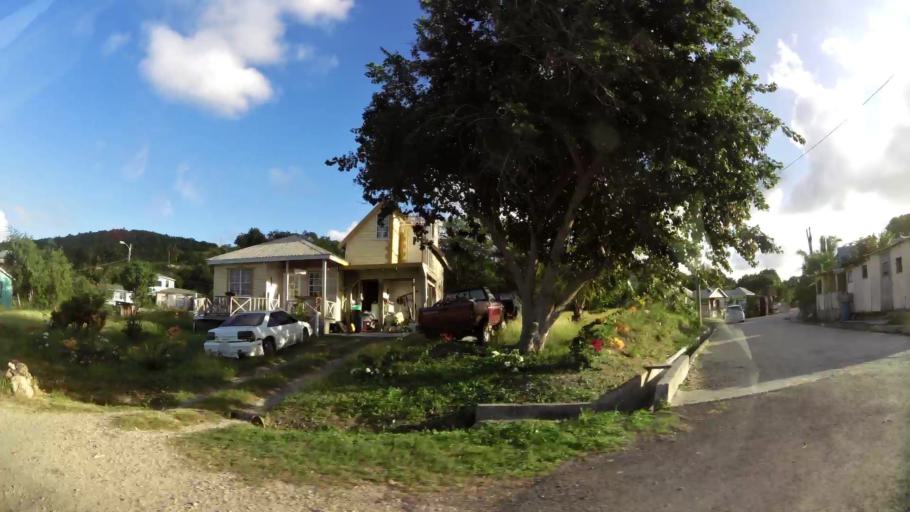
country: AG
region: Saint George
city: Piggotts
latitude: 17.1277
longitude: -61.8049
